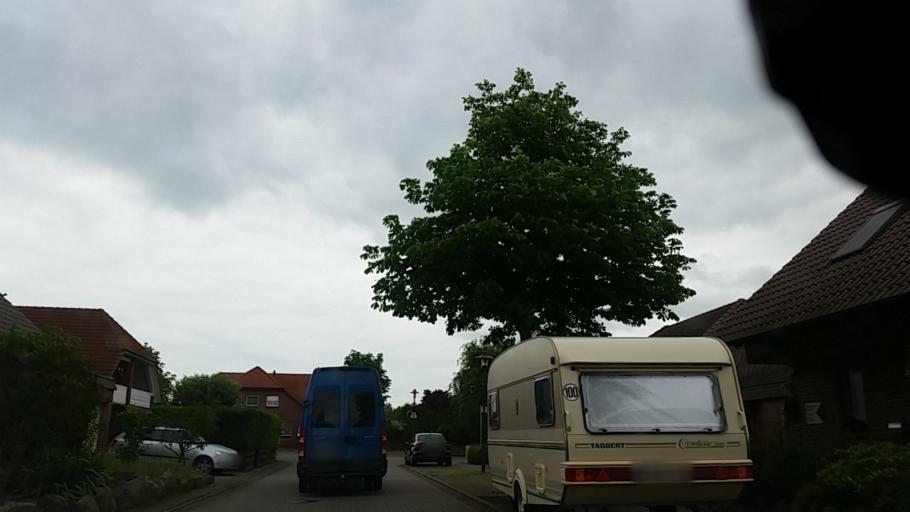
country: DE
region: Lower Saxony
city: Wolfsburg
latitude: 52.4113
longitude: 10.8435
